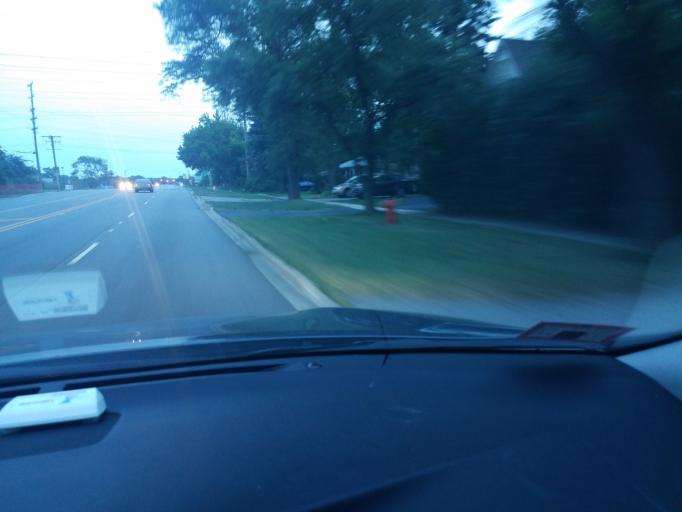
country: US
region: Illinois
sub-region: Cook County
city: Northbrook
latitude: 42.1379
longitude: -87.7957
